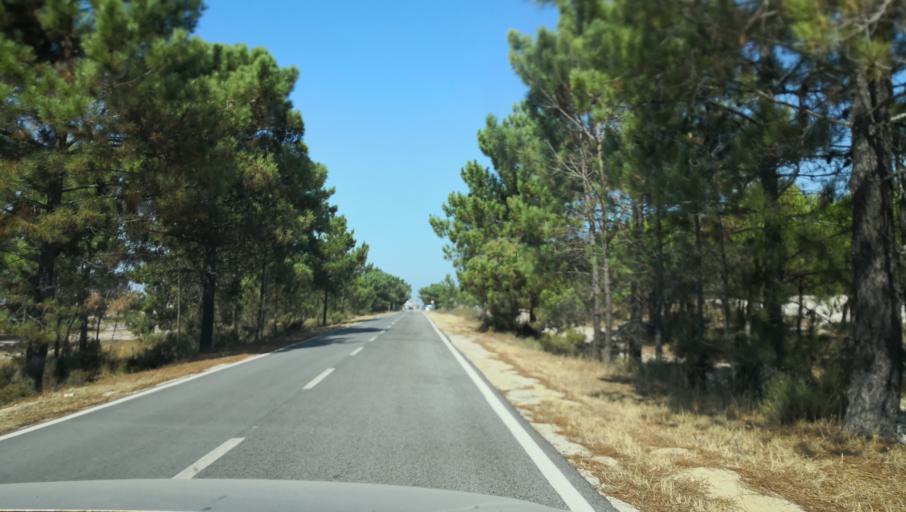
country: PT
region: Setubal
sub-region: Setubal
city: Setubal
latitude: 38.4046
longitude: -8.7458
